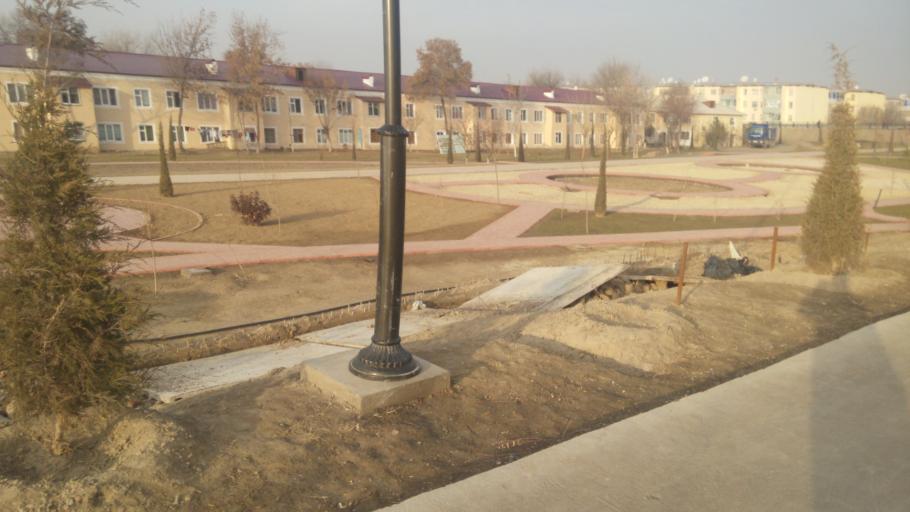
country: UZ
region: Sirdaryo
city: Guliston
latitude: 40.5098
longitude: 68.7777
